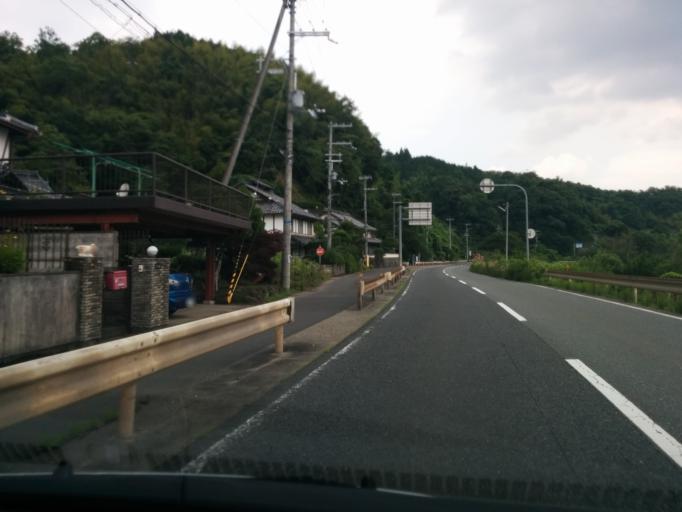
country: JP
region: Kyoto
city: Fukuchiyama
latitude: 35.3650
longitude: 135.1158
